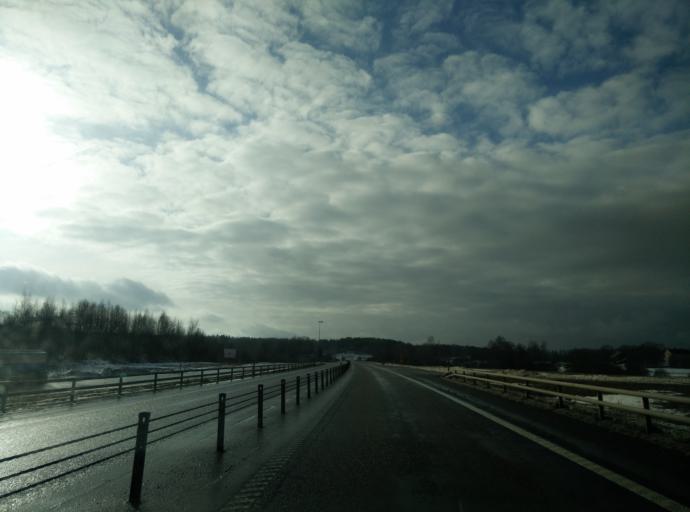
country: SE
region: Gaevleborg
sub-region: Sandvikens Kommun
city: Jarbo
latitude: 60.5813
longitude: 16.5388
